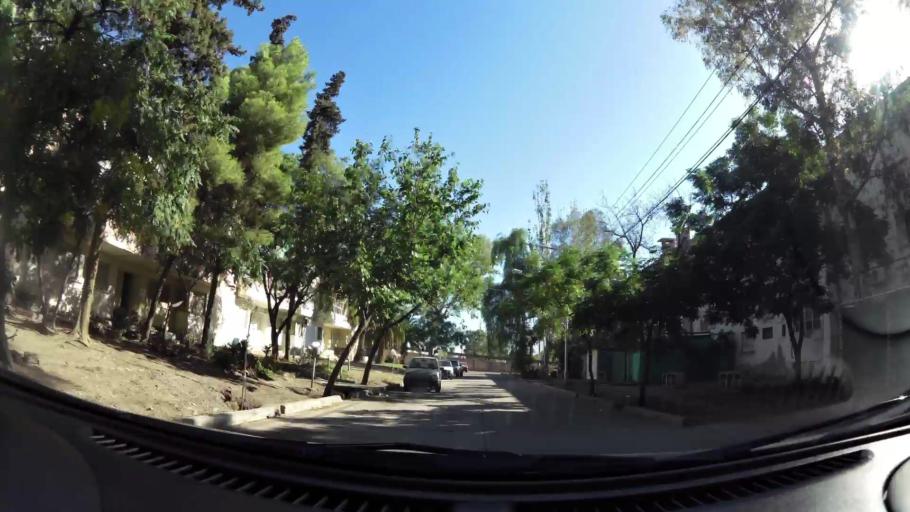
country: AR
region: Mendoza
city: Las Heras
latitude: -32.8691
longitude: -68.8606
